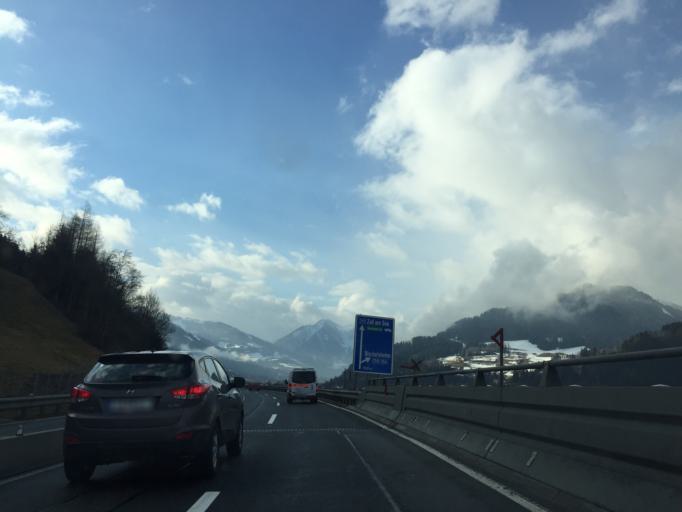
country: AT
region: Salzburg
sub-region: Politischer Bezirk Sankt Johann im Pongau
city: Bischofshofen
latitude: 47.4138
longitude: 13.2232
